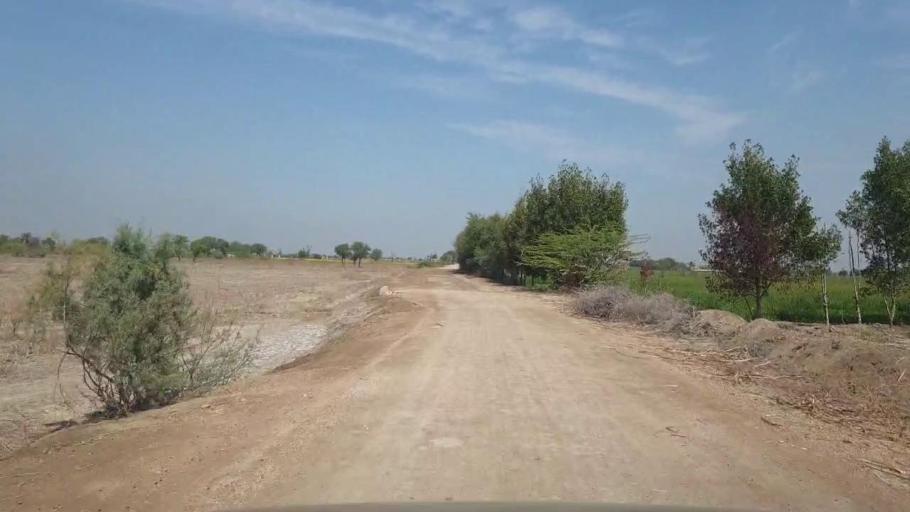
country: PK
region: Sindh
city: Mirwah Gorchani
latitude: 25.4332
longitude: 69.1864
